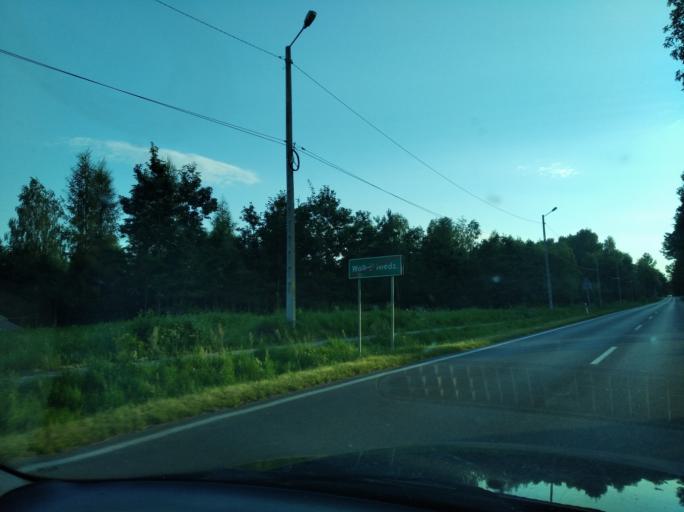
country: PL
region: Subcarpathian Voivodeship
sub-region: Powiat rzeszowski
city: Wolka Niedzwiedzka
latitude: 50.2403
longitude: 22.1821
